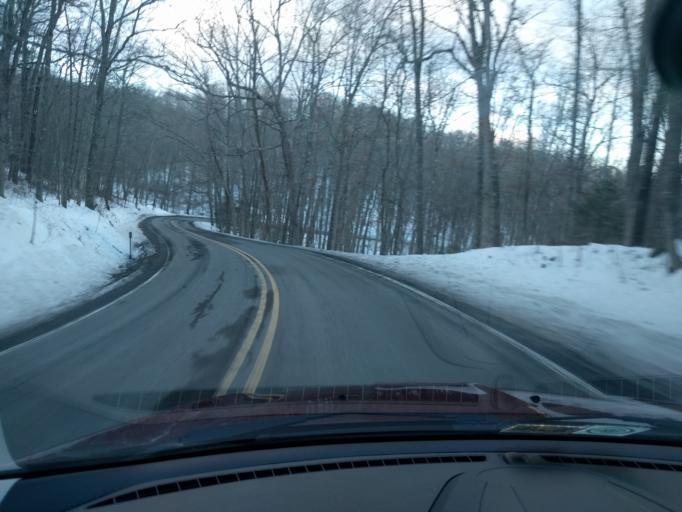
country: US
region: Virginia
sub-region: Bath County
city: Warm Springs
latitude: 38.0975
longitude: -79.8498
